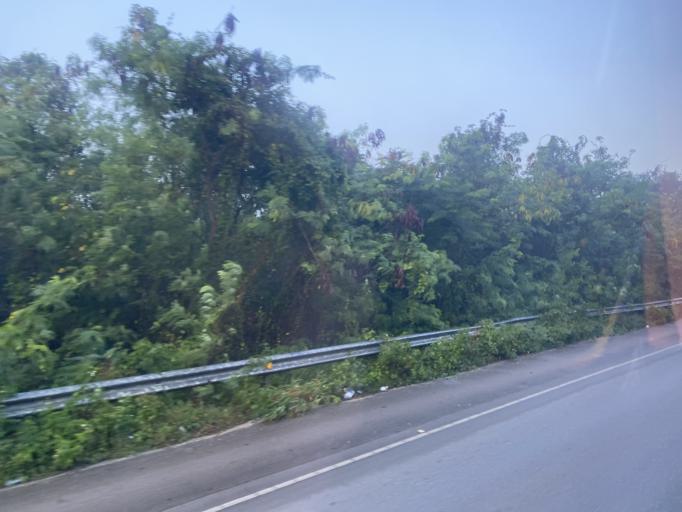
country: DO
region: La Altagracia
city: Otra Banda
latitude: 18.7386
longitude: -68.5129
